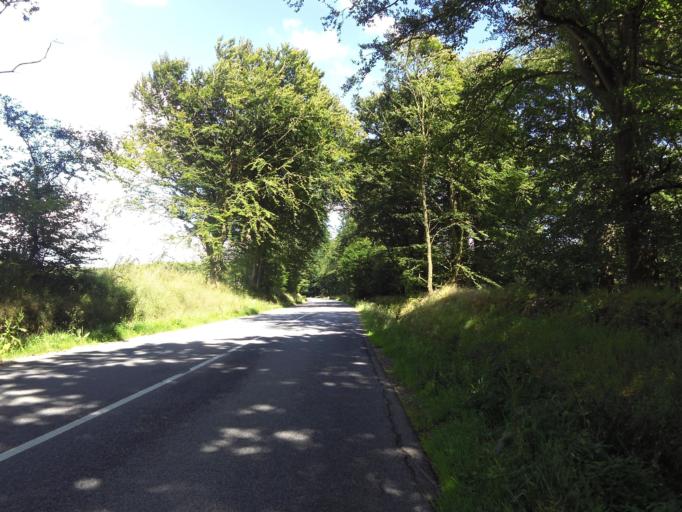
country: DK
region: South Denmark
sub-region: Haderslev Kommune
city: Gram
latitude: 55.3038
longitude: 9.0657
